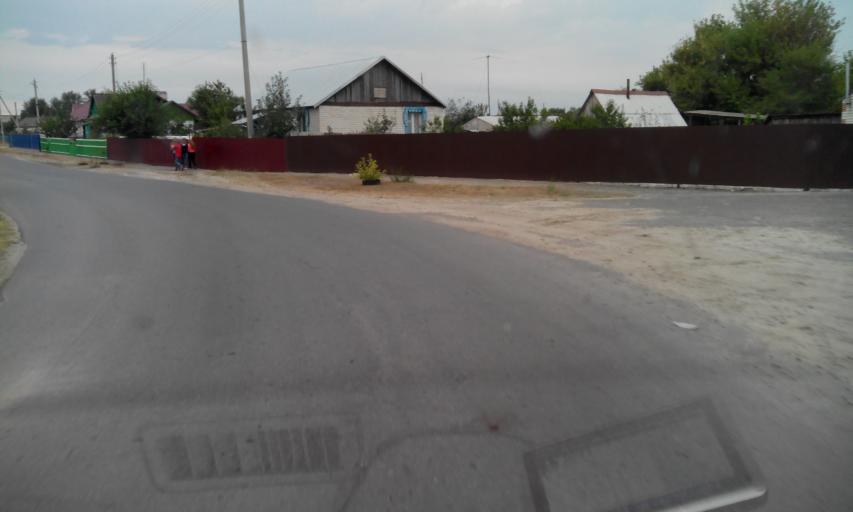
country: RU
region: Samara
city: Balasheyka
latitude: 53.1546
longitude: 48.1143
